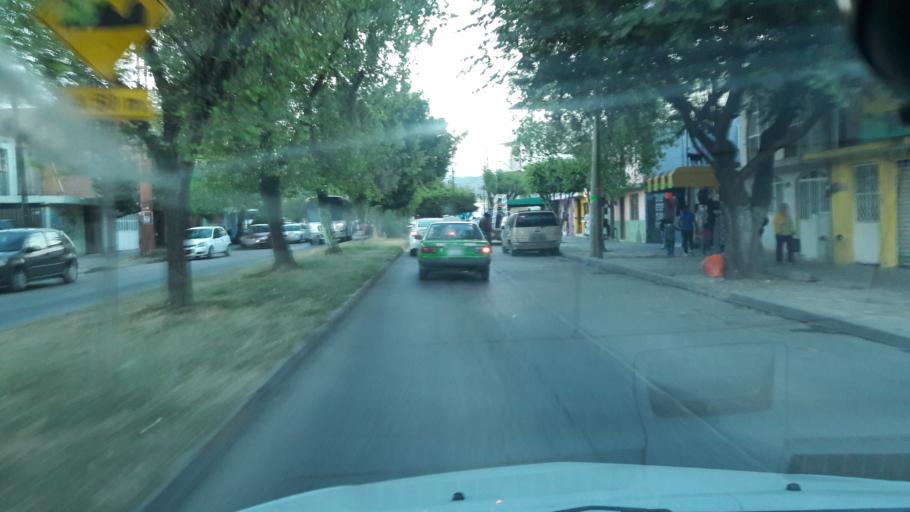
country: MX
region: Guanajuato
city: Leon
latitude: 21.1682
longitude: -101.6673
